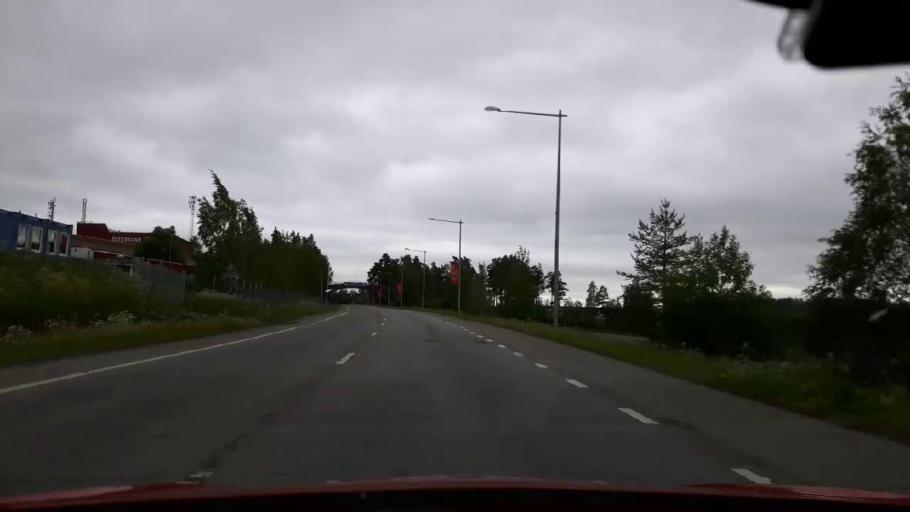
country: SE
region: Jaemtland
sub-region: OEstersunds Kommun
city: Ostersund
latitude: 63.1916
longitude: 14.6566
